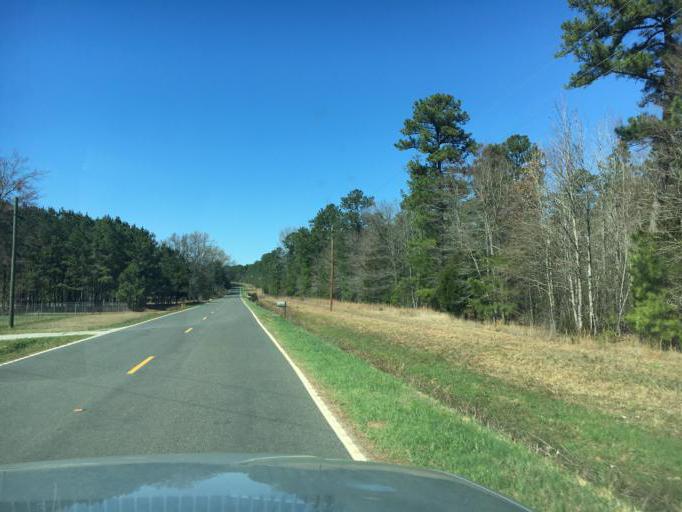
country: US
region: South Carolina
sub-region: Greenwood County
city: Ninety Six
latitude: 34.2843
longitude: -81.9545
